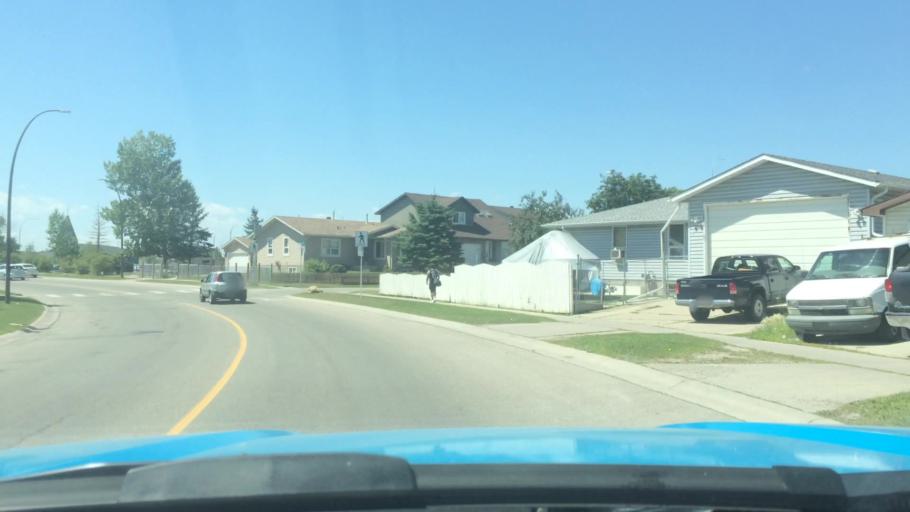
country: CA
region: Alberta
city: Calgary
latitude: 51.0469
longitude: -113.9917
